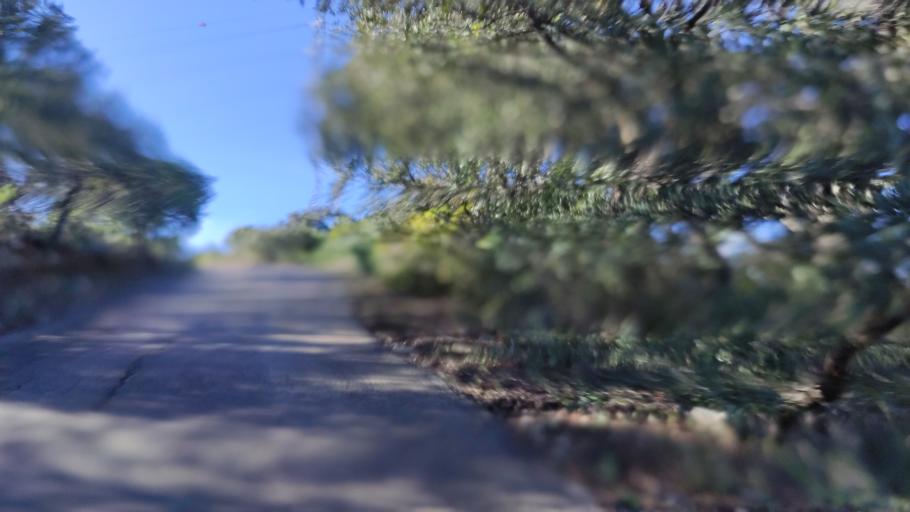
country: PT
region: Faro
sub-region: Sao Bras de Alportel
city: Sao Bras de Alportel
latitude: 37.1517
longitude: -7.8594
